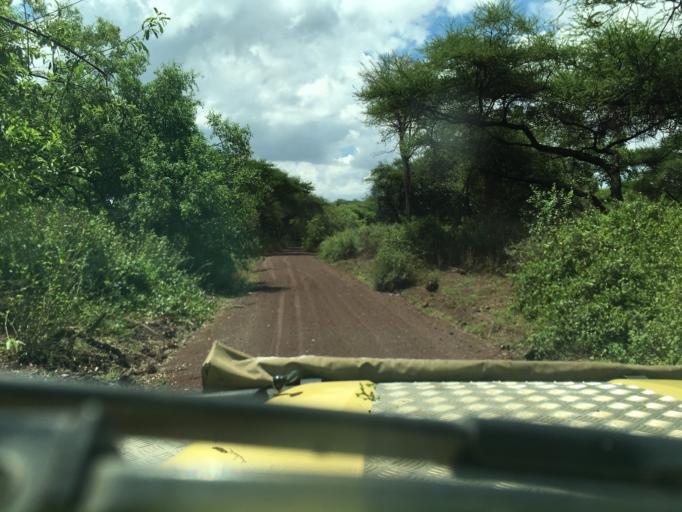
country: TZ
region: Arusha
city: Mto wa Mbu
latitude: -3.4231
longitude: 35.8144
